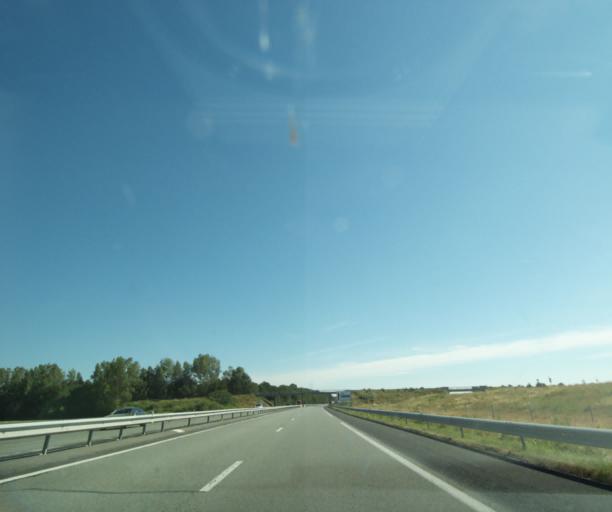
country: FR
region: Lorraine
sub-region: Departement des Vosges
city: Lamarche
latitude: 48.1302
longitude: 5.6696
